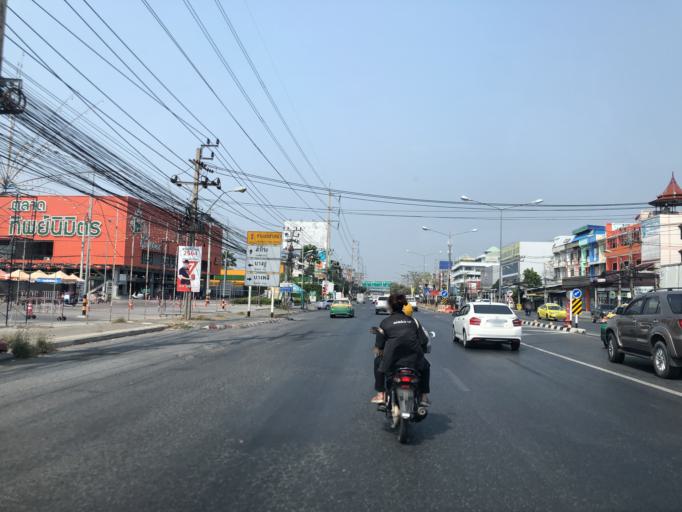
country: TH
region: Bangkok
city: Bang Na
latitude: 13.6025
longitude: 100.7059
